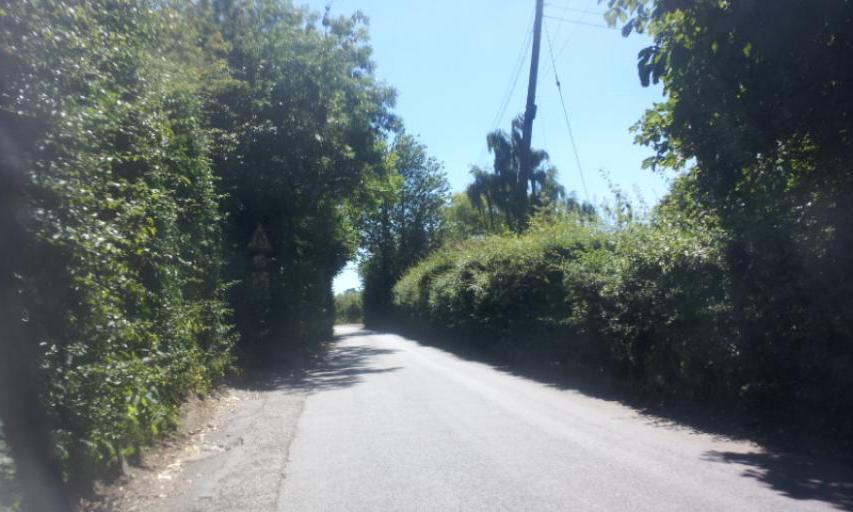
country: GB
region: England
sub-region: Kent
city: Newington
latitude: 51.3158
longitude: 0.6934
